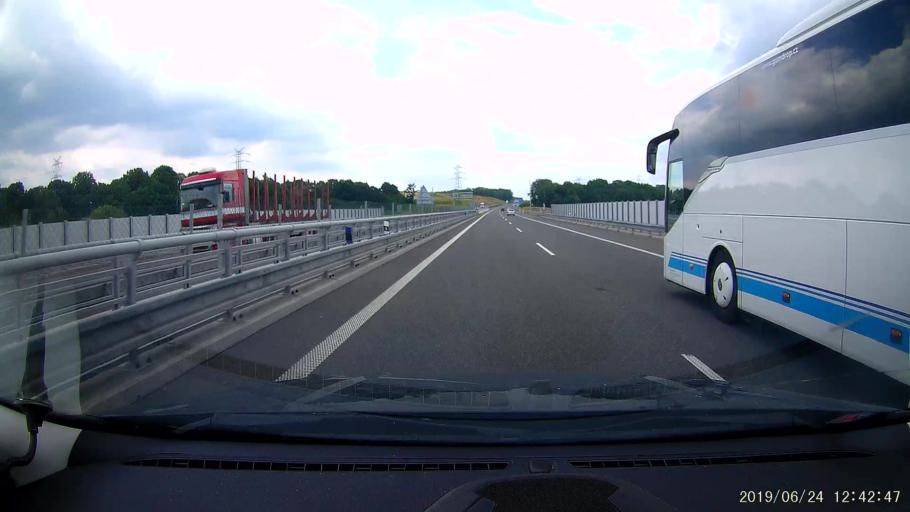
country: PL
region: Silesian Voivodeship
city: Gorzyczki
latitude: 49.9348
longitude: 18.4041
